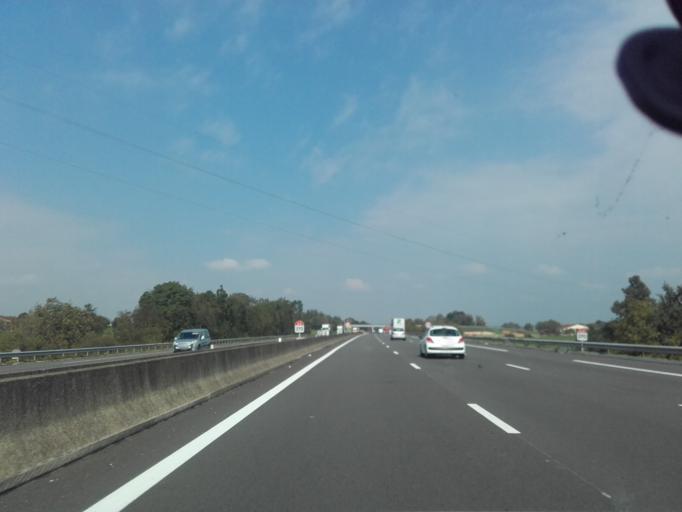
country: FR
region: Rhone-Alpes
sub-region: Departement de l'Ain
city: Pont-de-Vaux
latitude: 46.4613
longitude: 4.8771
